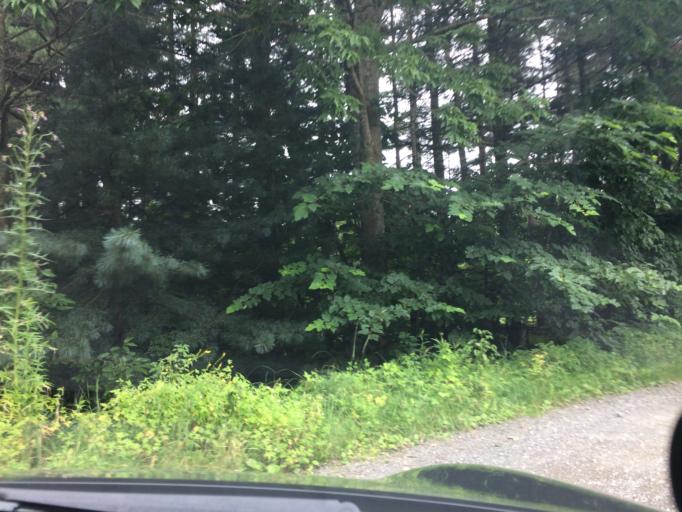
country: JP
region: Hokkaido
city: Otofuke
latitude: 42.9614
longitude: 143.1230
